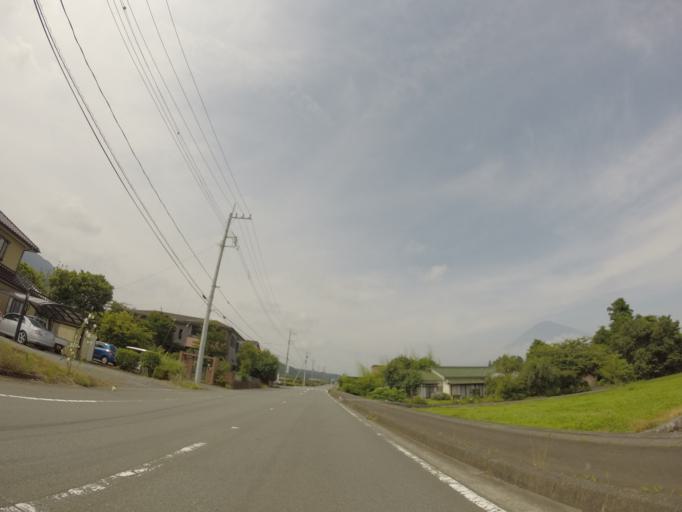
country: JP
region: Shizuoka
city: Fujinomiya
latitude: 35.2828
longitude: 138.5755
